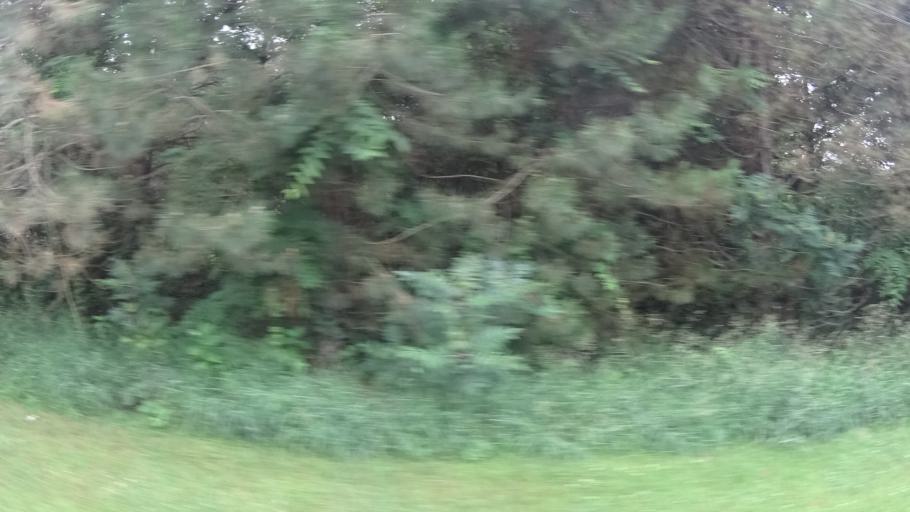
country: US
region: Ohio
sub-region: Erie County
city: Milan
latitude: 41.2959
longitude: -82.5351
